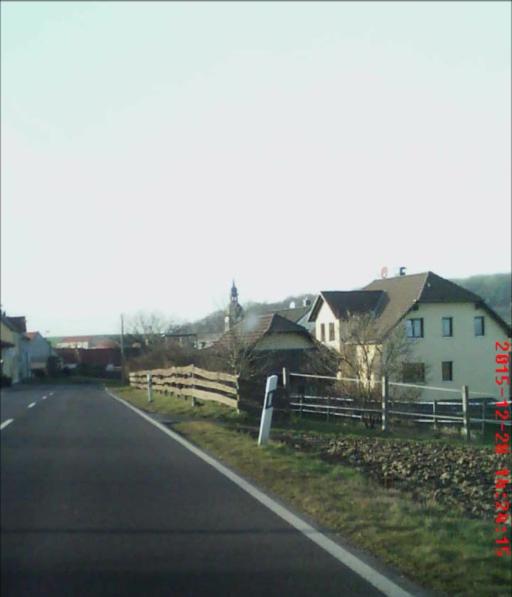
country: DE
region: Thuringia
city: Pfiffelbach
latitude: 51.0575
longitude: 11.4477
